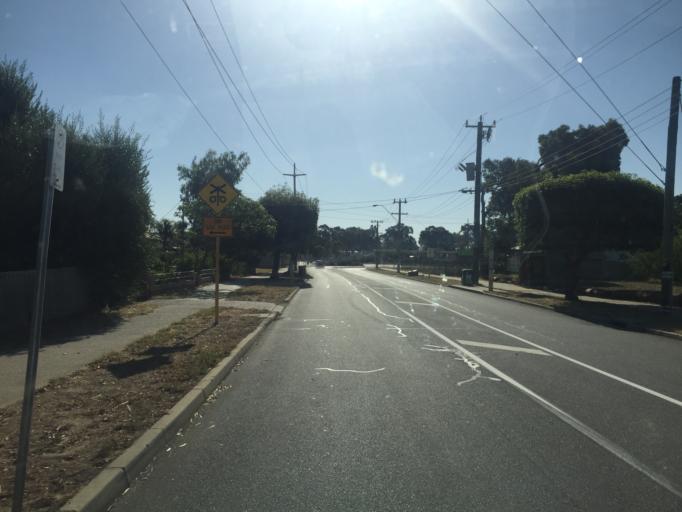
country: AU
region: Western Australia
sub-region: Gosnells
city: Kenwick
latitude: -32.0356
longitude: 115.9712
